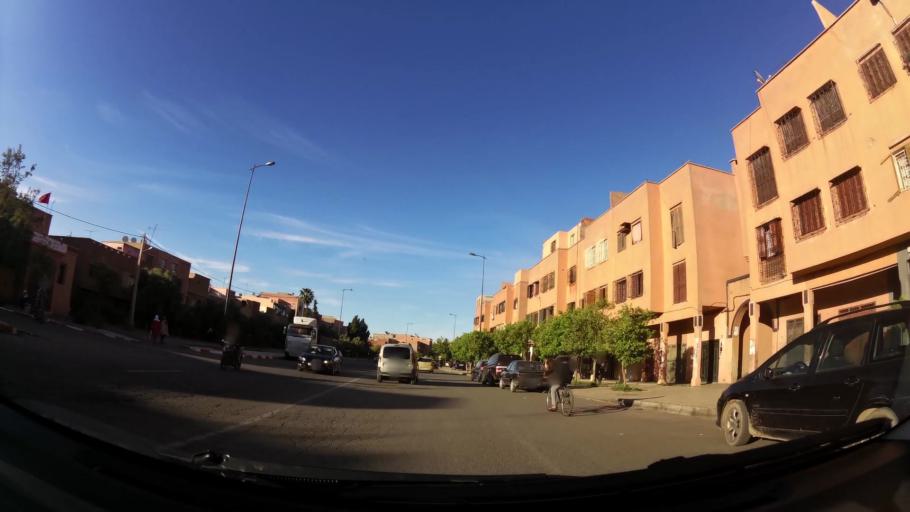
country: MA
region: Marrakech-Tensift-Al Haouz
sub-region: Marrakech
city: Marrakesh
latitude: 31.6207
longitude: -8.0575
